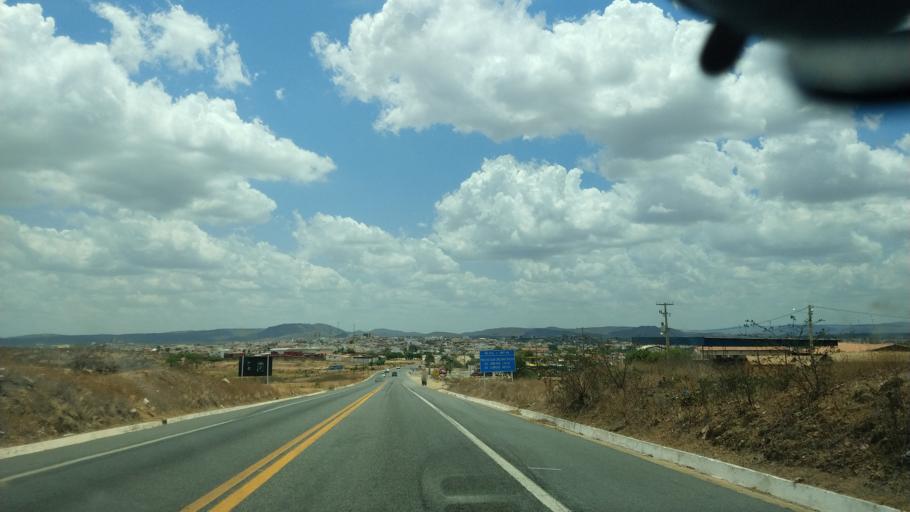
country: BR
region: Rio Grande do Norte
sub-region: Currais Novos
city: Currais Novos
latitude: -6.2578
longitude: -36.4982
